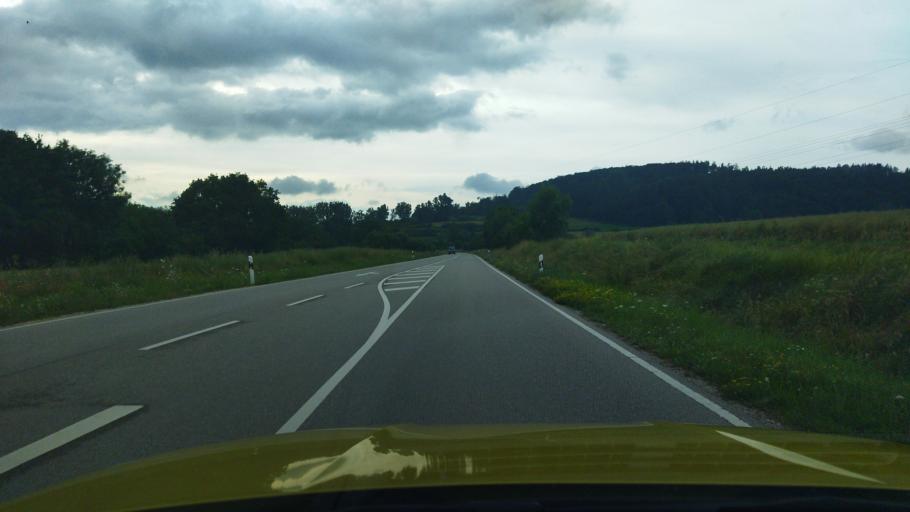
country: DE
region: Bavaria
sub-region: Regierungsbezirk Mittelfranken
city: Greding
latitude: 49.0637
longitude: 11.3249
